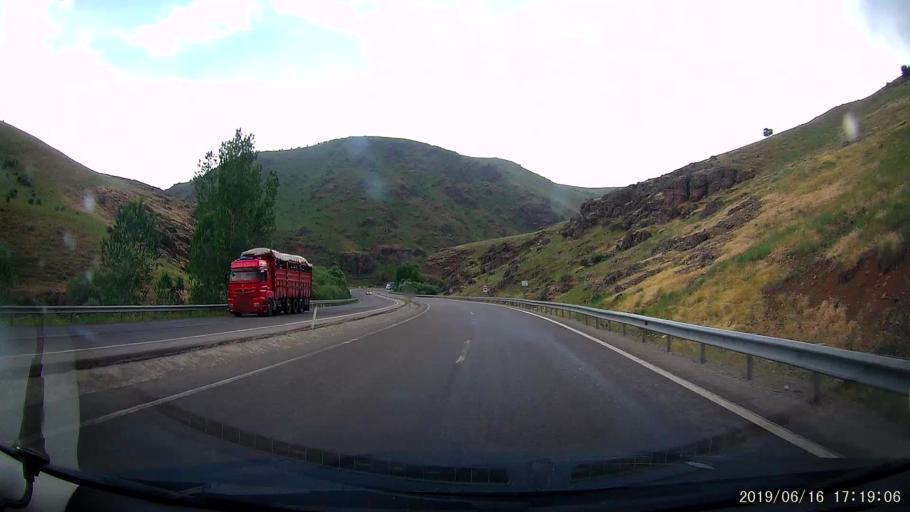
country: TR
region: Erzincan
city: Tercan
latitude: 39.8044
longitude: 40.5312
